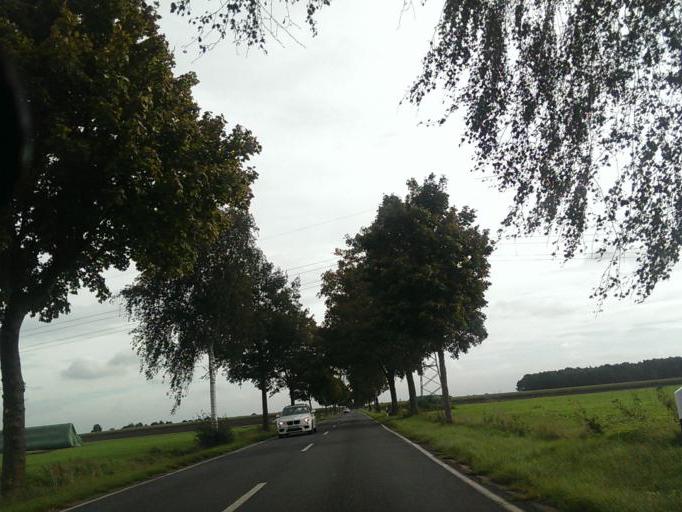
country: DE
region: Lower Saxony
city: Neustadt am Rubenberge
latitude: 52.4569
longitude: 9.4952
